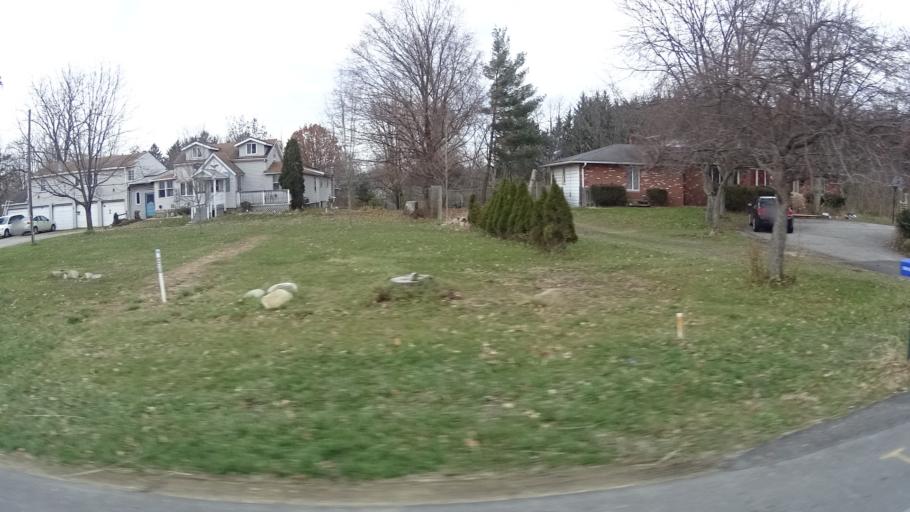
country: US
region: Ohio
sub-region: Cuyahoga County
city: Strongsville
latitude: 41.3126
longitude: -81.8951
